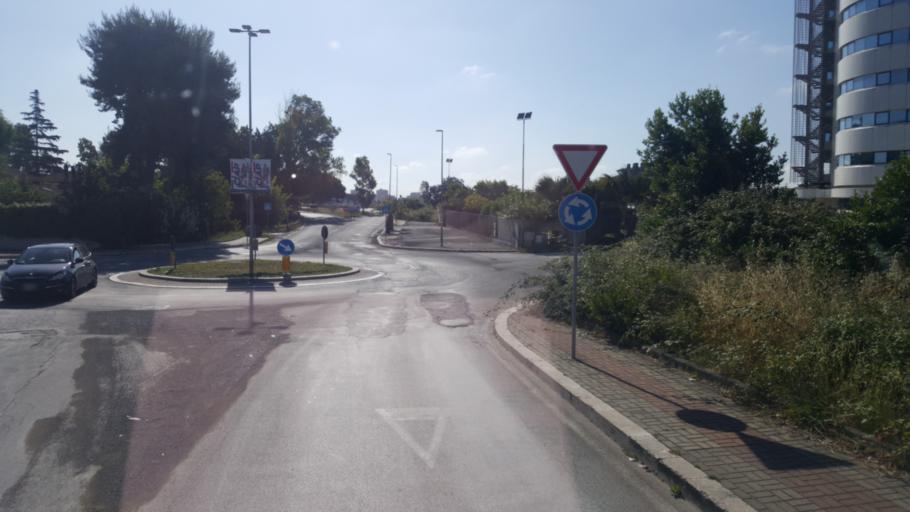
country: IT
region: Latium
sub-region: Provincia di Latina
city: Aprilia
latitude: 41.5784
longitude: 12.6488
